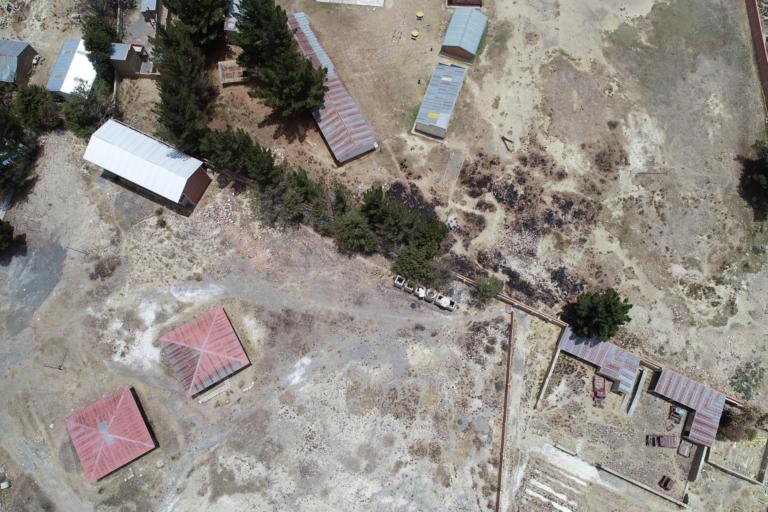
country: BO
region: La Paz
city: Achacachi
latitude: -16.0439
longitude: -68.6910
